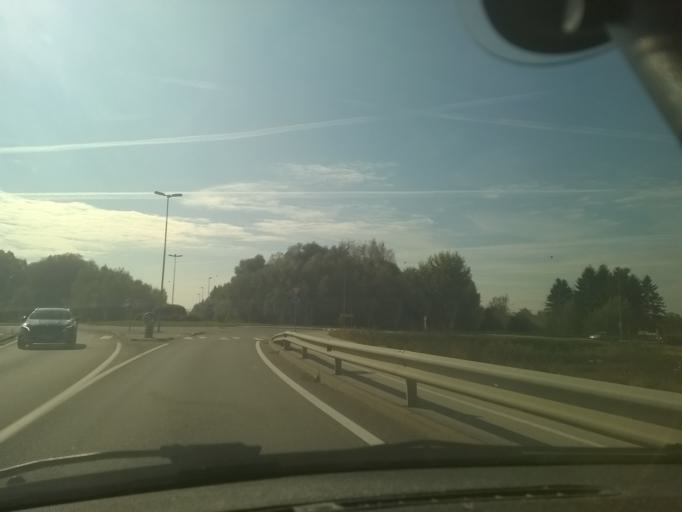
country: SI
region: Ptuj
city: Ptuj
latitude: 46.4076
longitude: 15.8768
